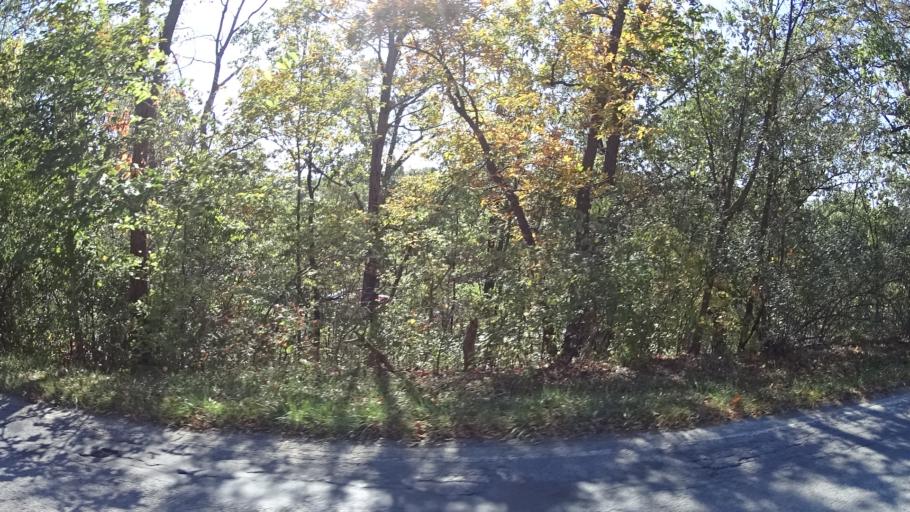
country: US
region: Ohio
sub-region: Lorain County
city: Vermilion
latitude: 41.4143
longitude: -82.3436
